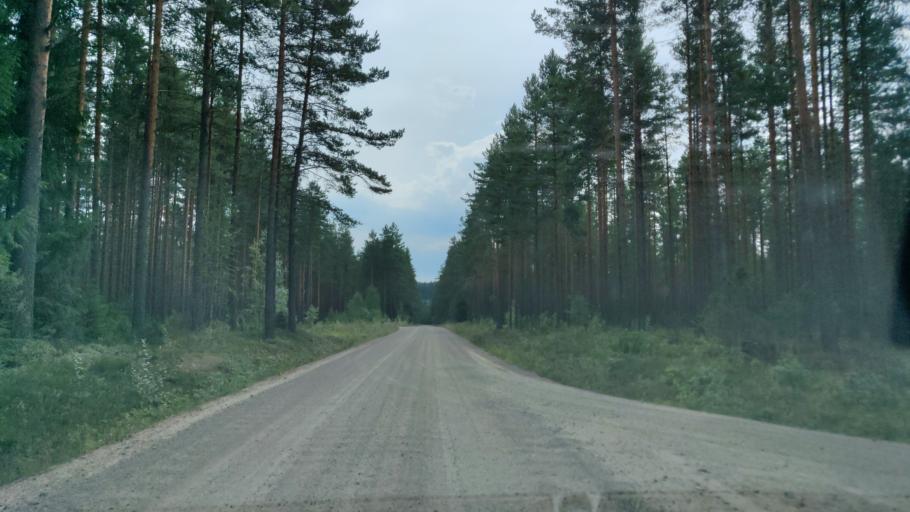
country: SE
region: Vaermland
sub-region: Munkfors Kommun
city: Munkfors
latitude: 59.9508
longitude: 13.5078
